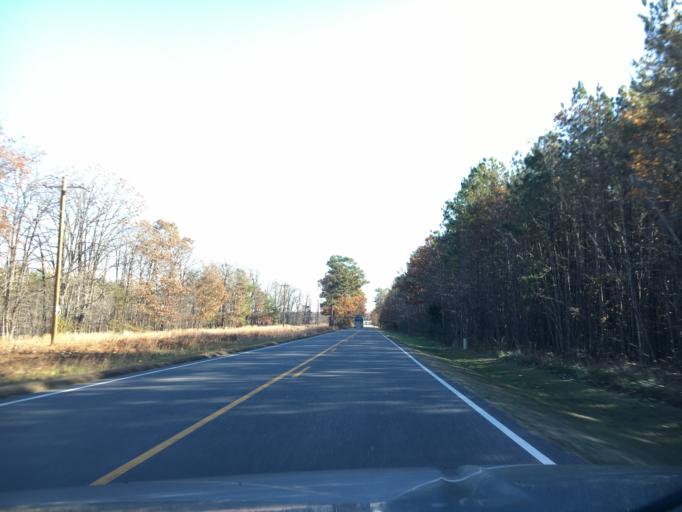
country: US
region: Virginia
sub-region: Appomattox County
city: Appomattox
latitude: 37.4559
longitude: -78.6981
